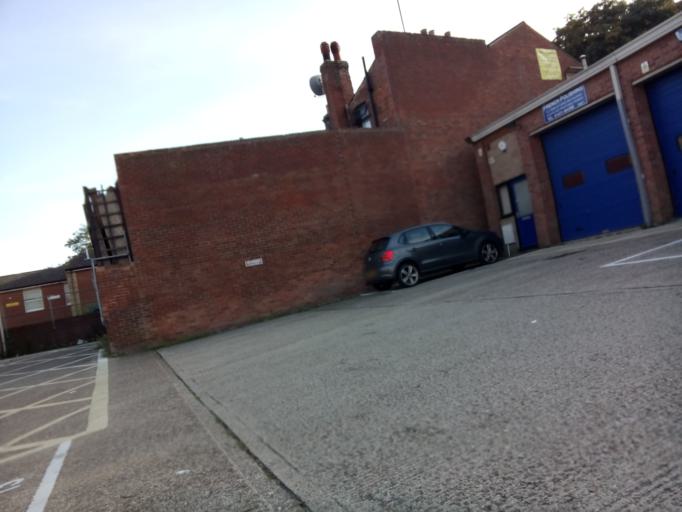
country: GB
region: England
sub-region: Suffolk
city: Ipswich
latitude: 52.0506
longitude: 1.1551
